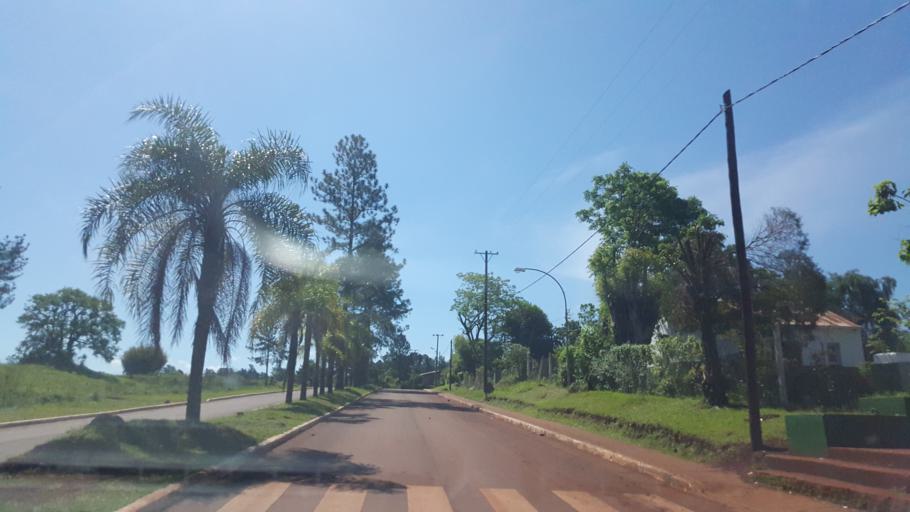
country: AR
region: Misiones
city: Garupa
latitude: -27.5072
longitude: -55.8552
